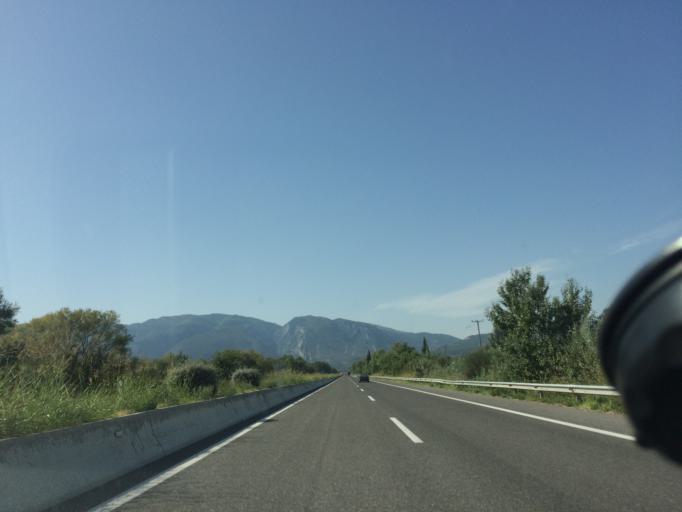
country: GR
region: Thessaly
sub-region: Nomos Larisis
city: Pyrgetos
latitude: 39.9300
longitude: 22.6410
